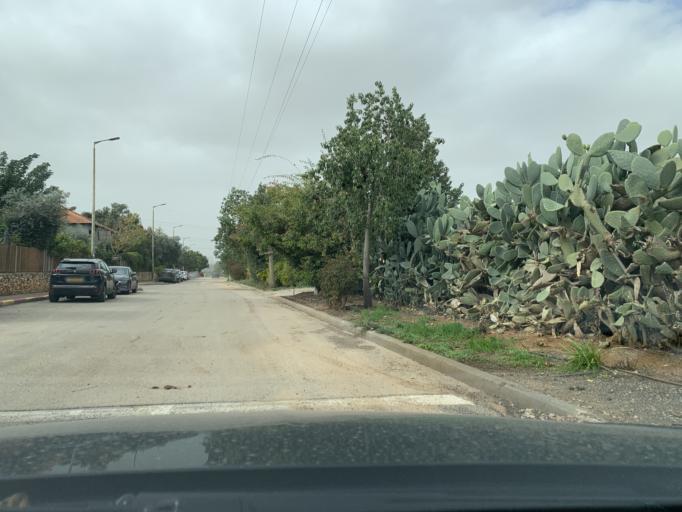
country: IL
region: Central District
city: Jaljulya
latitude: 32.1586
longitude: 34.9414
